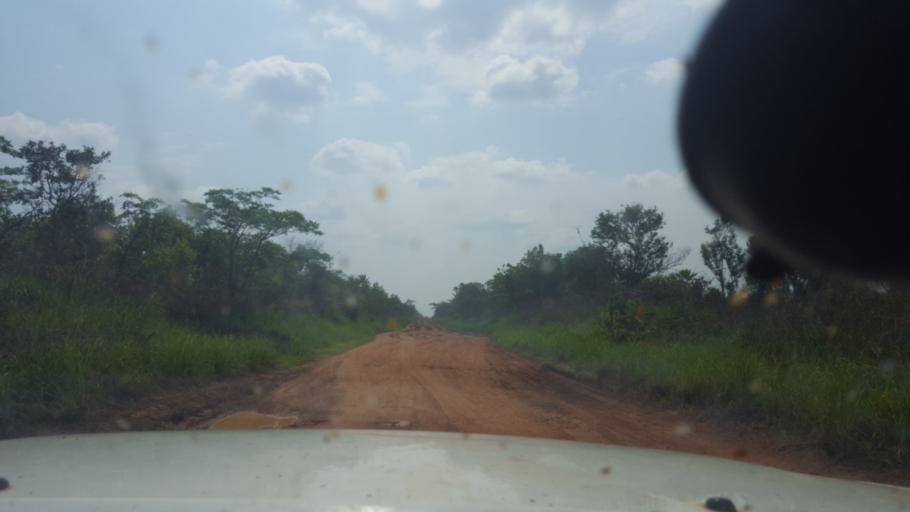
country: CD
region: Bandundu
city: Bandundu
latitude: -3.7620
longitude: 17.1452
